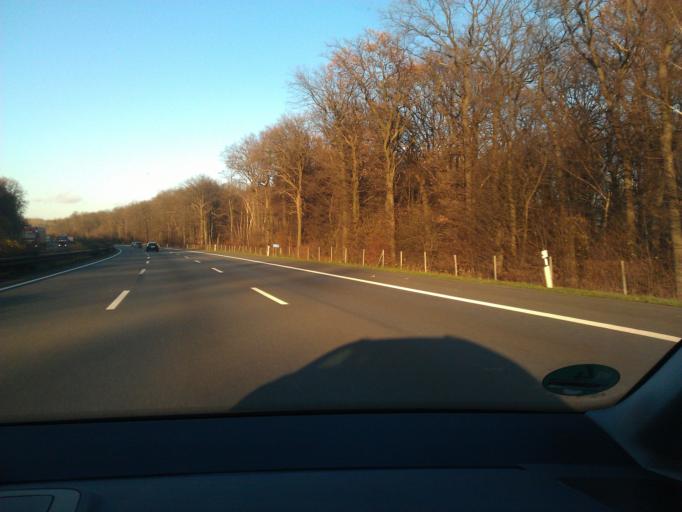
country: DE
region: North Rhine-Westphalia
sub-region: Regierungsbezirk Munster
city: Beckum
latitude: 51.7027
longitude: 7.9771
